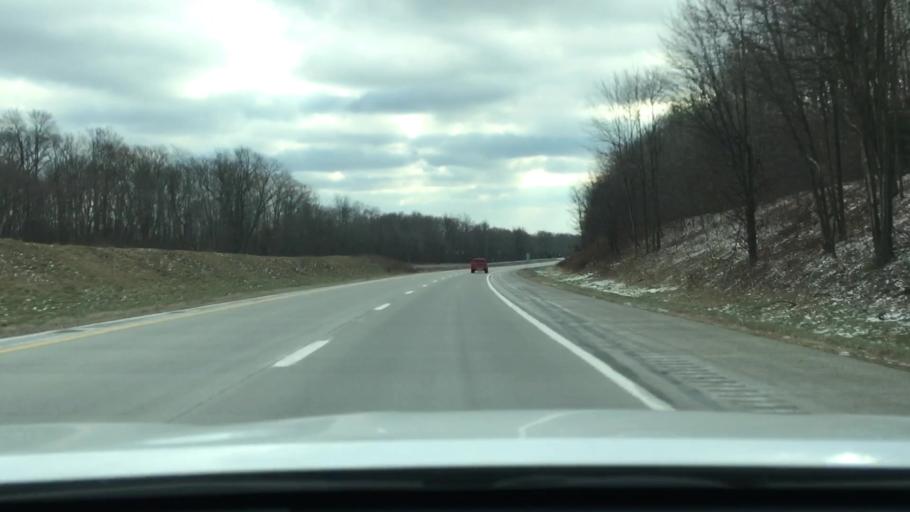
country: US
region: Pennsylvania
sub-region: Monroe County
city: Mount Pocono
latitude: 41.1425
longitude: -75.4029
